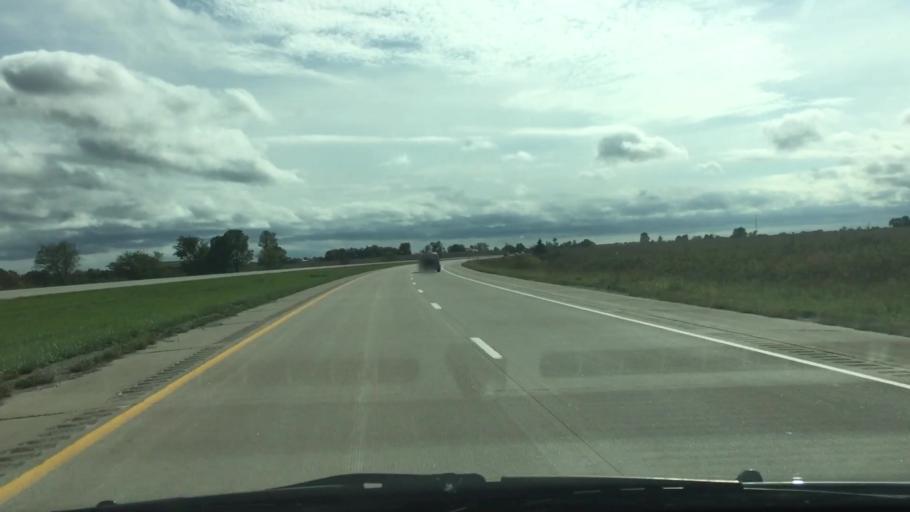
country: US
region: Iowa
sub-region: Decatur County
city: Leon
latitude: 40.8446
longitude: -93.8047
